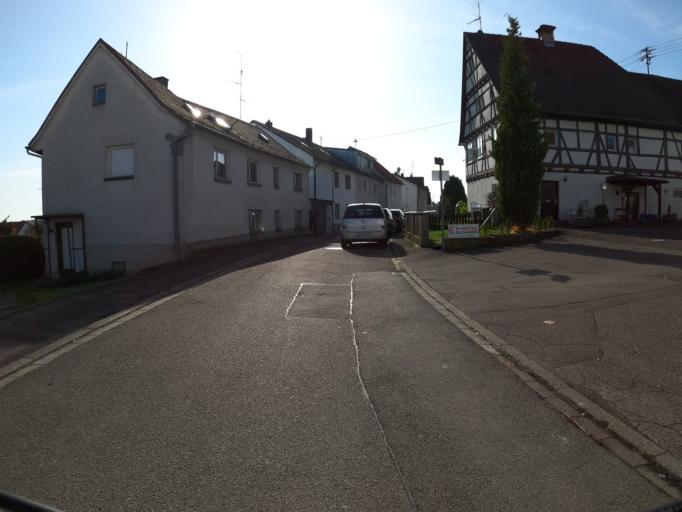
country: DE
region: Bavaria
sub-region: Swabia
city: Nersingen
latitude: 48.4593
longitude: 10.1029
